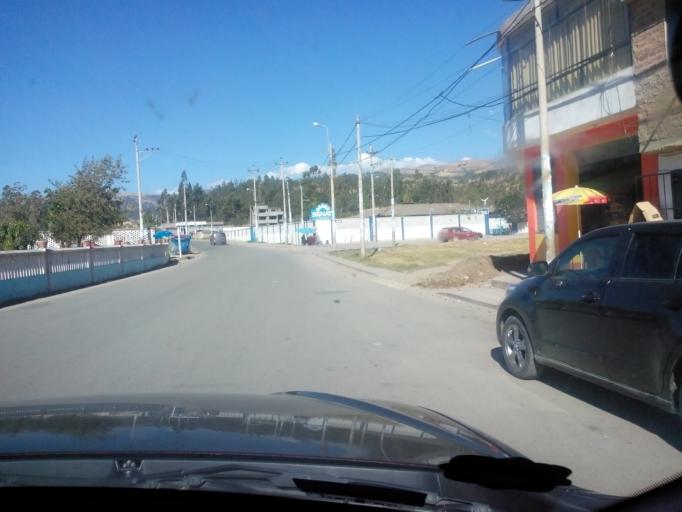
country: PE
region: Apurimac
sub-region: Provincia de Andahuaylas
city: Talavera
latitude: -13.6582
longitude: -73.4302
